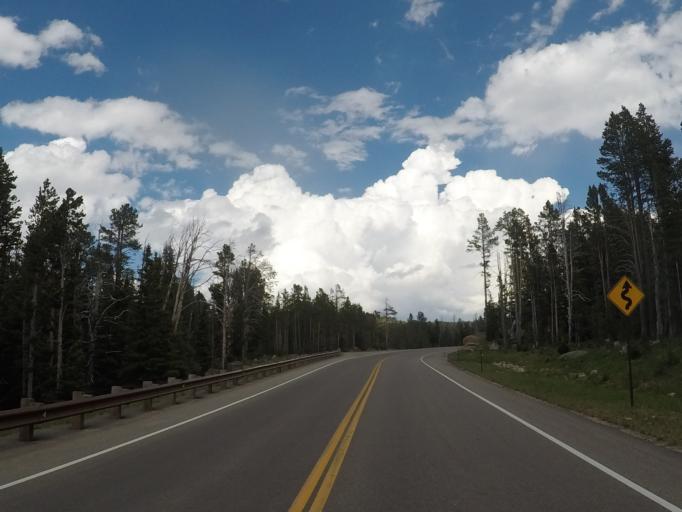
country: US
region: Montana
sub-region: Carbon County
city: Red Lodge
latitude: 44.9444
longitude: -109.5698
